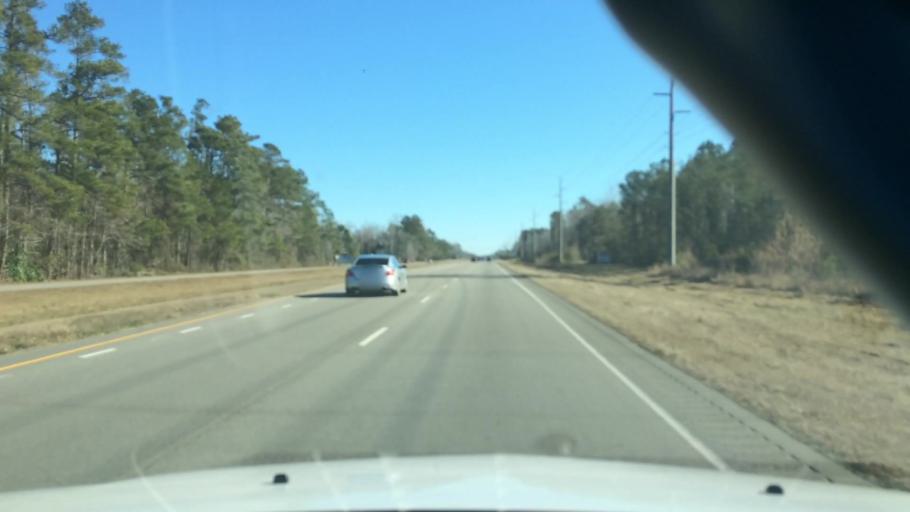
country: US
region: North Carolina
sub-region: Brunswick County
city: Shallotte
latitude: 34.0024
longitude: -78.3151
